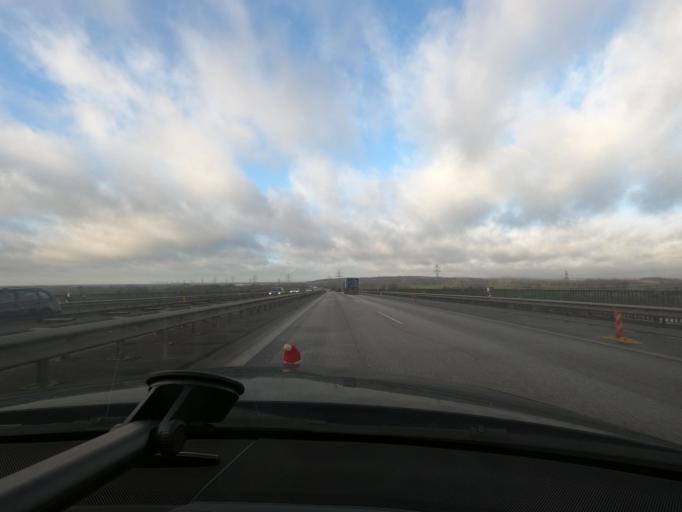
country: DE
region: Schleswig-Holstein
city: Borgstedt
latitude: 54.3339
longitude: 9.7232
